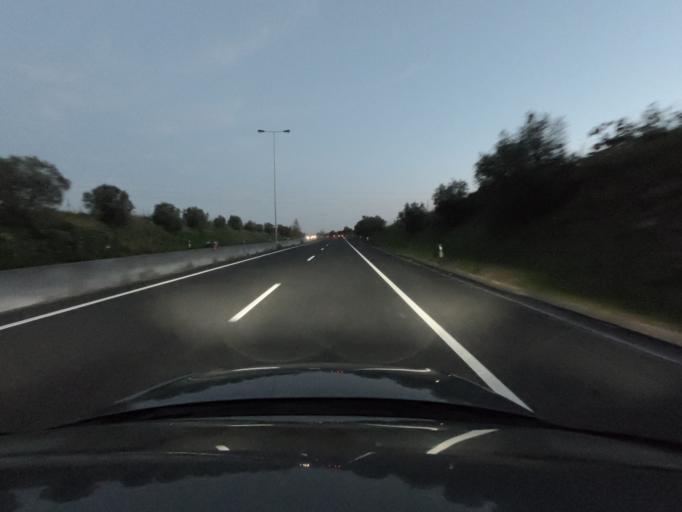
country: PT
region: Lisbon
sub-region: Oeiras
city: Porto Salvo
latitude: 38.7265
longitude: -9.2963
